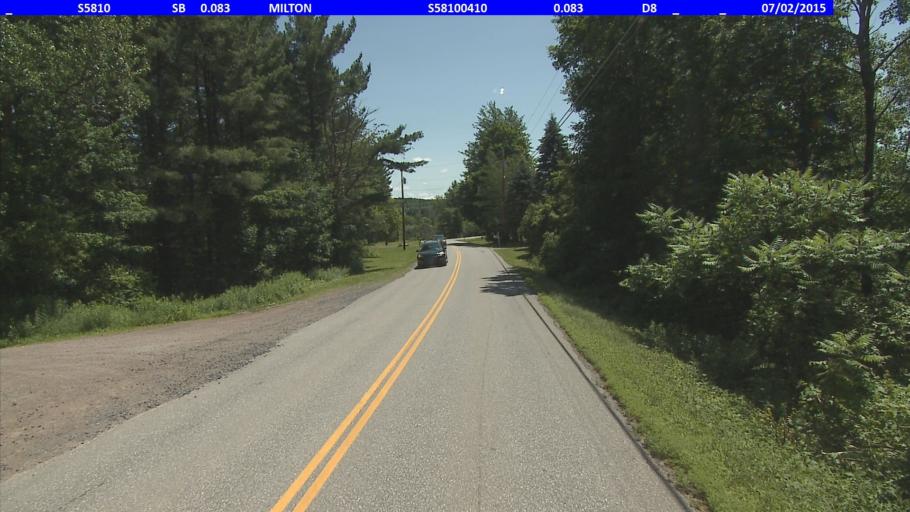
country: US
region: Vermont
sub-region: Chittenden County
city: Colchester
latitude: 44.5831
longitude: -73.1287
